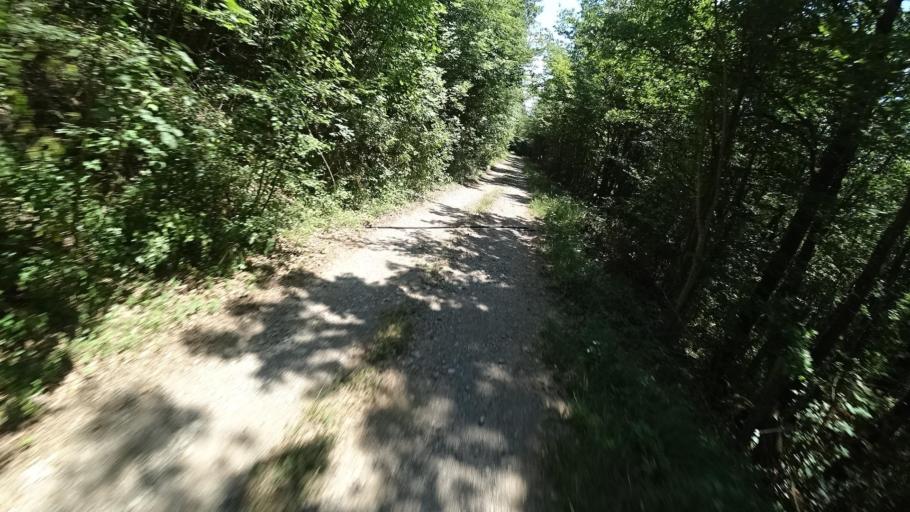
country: HR
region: Karlovacka
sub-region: Grad Ogulin
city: Ogulin
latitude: 45.3210
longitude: 15.2383
